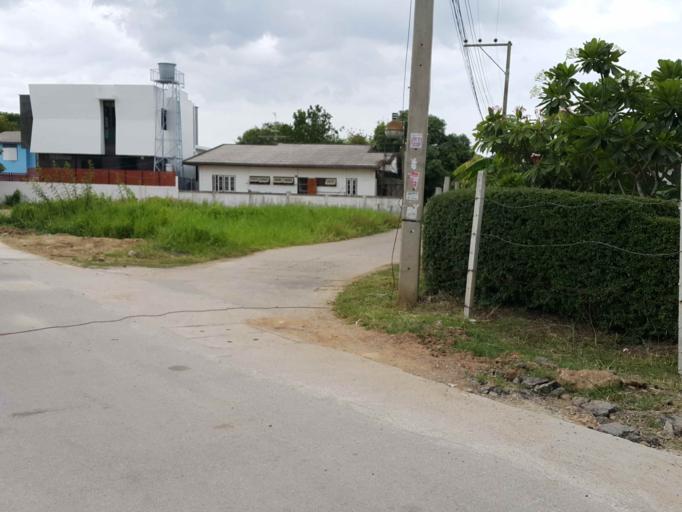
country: TH
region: Chiang Mai
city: Chiang Mai
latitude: 18.7539
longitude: 99.0040
